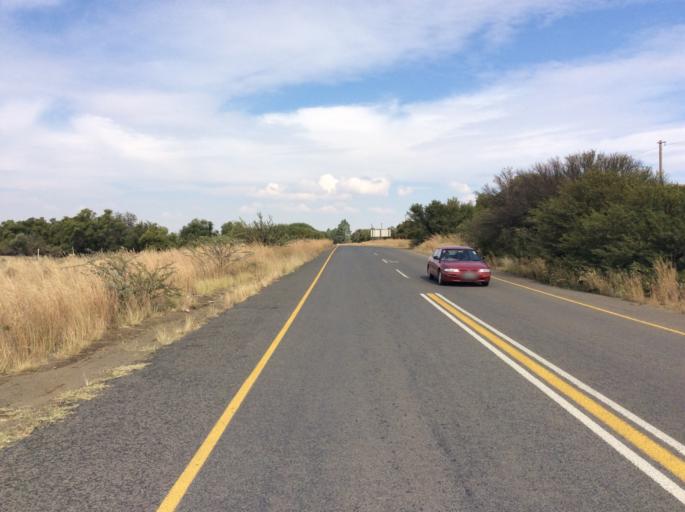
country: ZA
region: Orange Free State
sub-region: Xhariep District Municipality
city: Dewetsdorp
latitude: -29.5630
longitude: 26.6662
